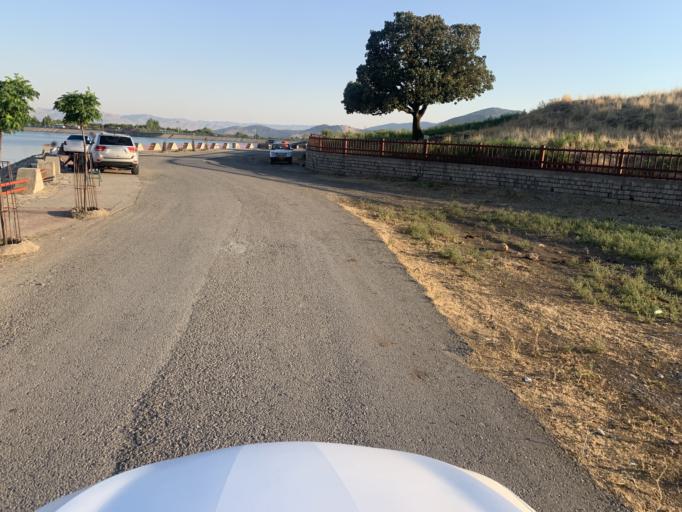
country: IQ
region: As Sulaymaniyah
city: Raniye
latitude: 36.2743
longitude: 44.7538
